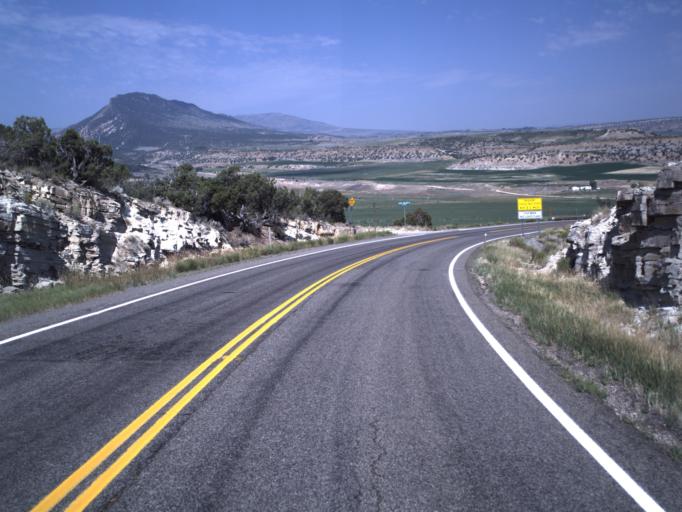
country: US
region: Utah
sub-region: Daggett County
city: Manila
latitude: 40.9385
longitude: -109.7098
